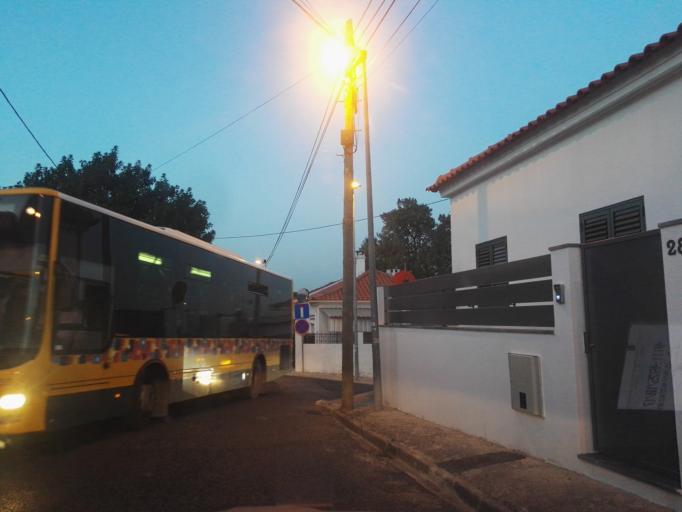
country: PT
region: Lisbon
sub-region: Lisbon
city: Lisbon
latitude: 38.7336
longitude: -9.1715
